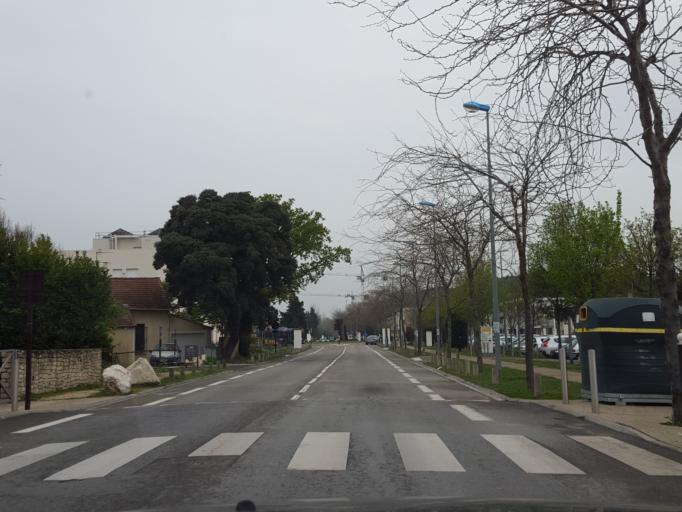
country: FR
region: Provence-Alpes-Cote d'Azur
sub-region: Departement du Vaucluse
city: Montfavet
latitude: 43.9155
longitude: 4.8909
